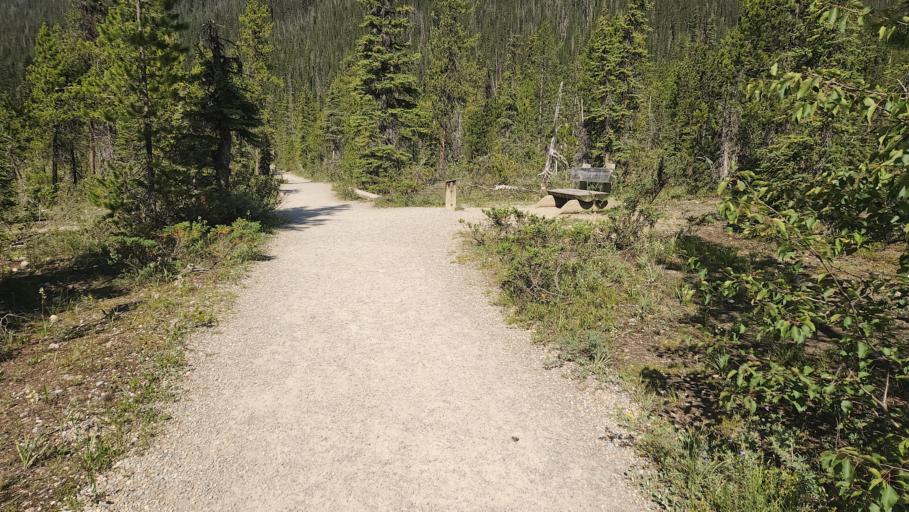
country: CA
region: Alberta
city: Lake Louise
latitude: 51.4510
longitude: -116.5294
